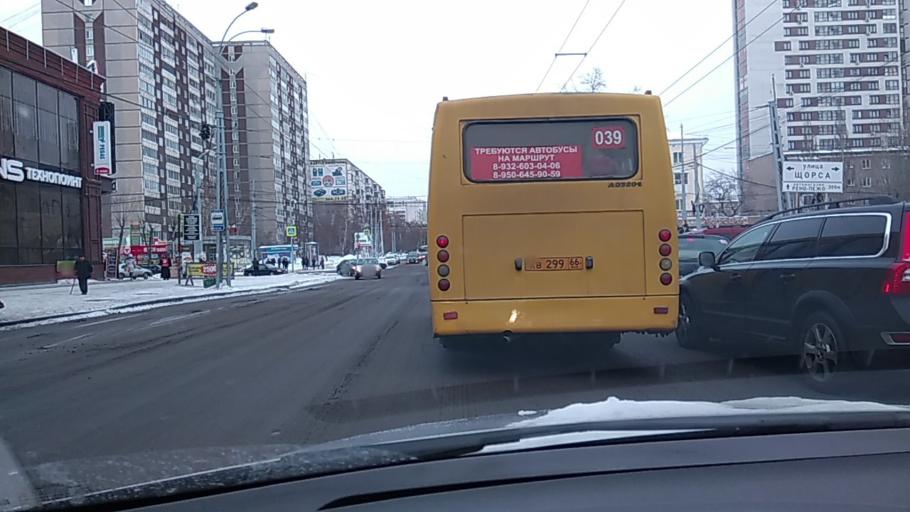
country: RU
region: Sverdlovsk
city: Yekaterinburg
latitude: 56.8092
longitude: 60.6232
